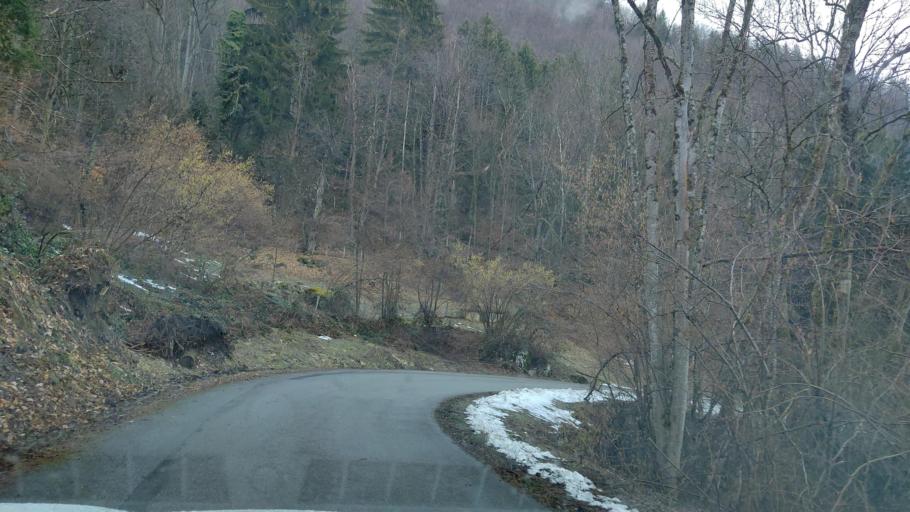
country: FR
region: Rhone-Alpes
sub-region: Departement de la Savoie
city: Aiton
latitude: 45.5116
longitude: 6.2831
